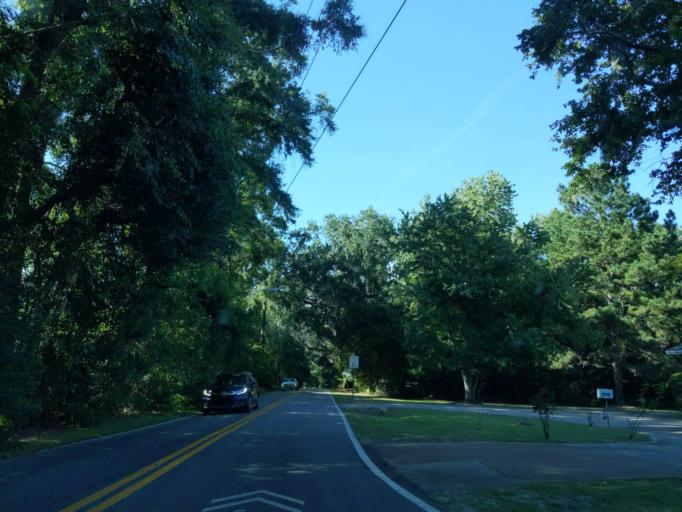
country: US
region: Florida
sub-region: Leon County
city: Tallahassee
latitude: 30.4126
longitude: -84.2437
